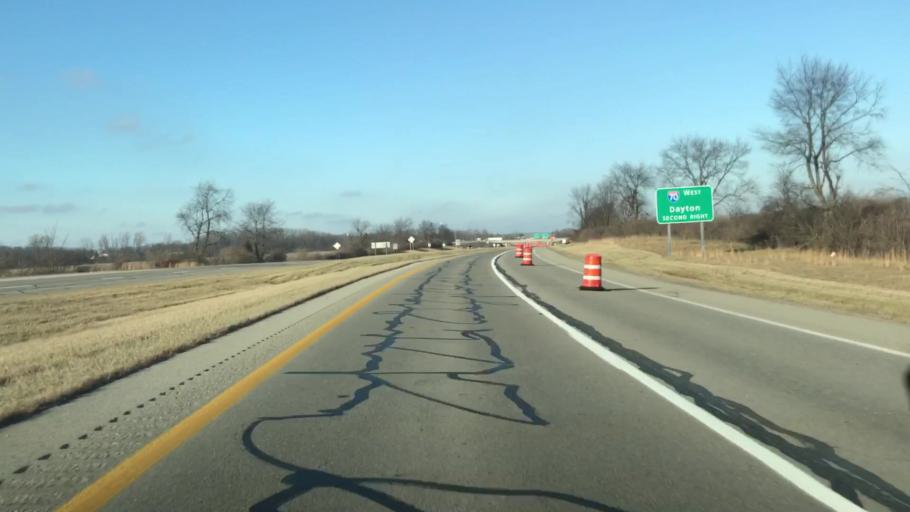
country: US
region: Ohio
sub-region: Clark County
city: Springfield
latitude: 39.8862
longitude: -83.8543
